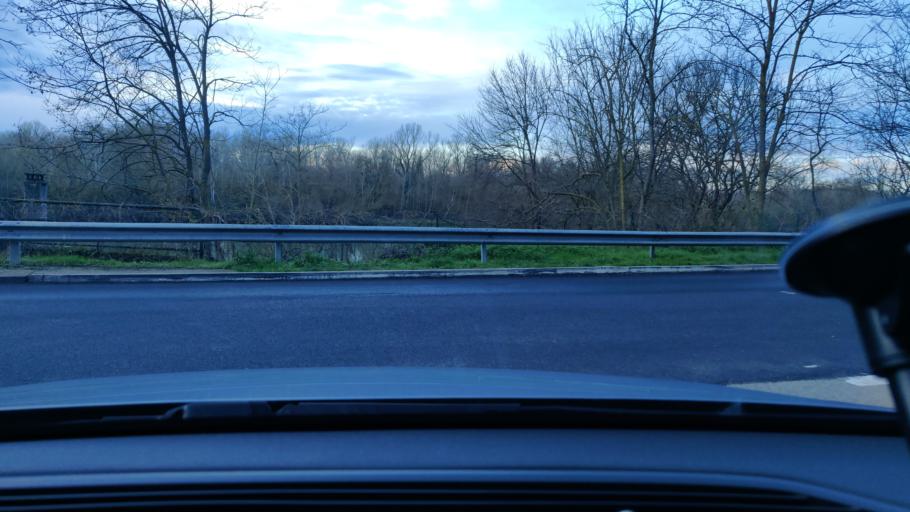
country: FR
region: Midi-Pyrenees
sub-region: Departement de la Haute-Garonne
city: Vieille-Toulouse
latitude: 43.5495
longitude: 1.4398
